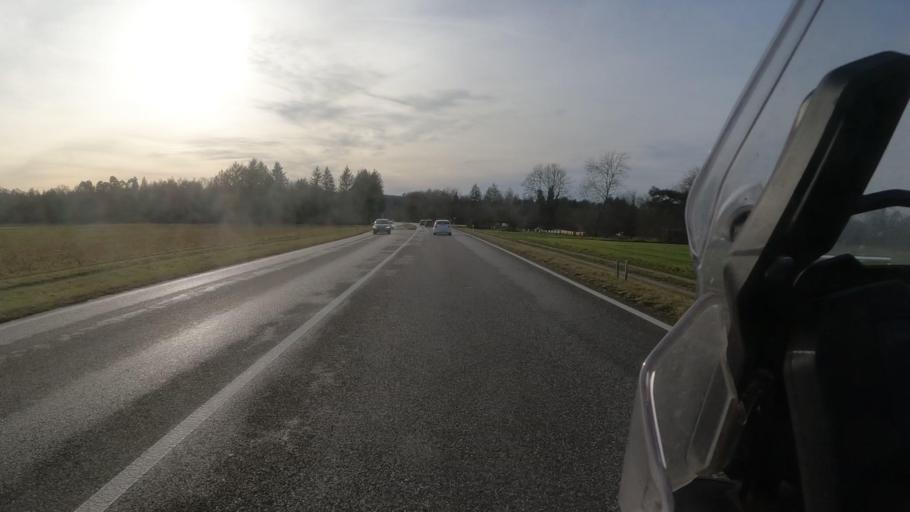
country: CH
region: Zurich
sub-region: Bezirk Buelach
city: Rafz
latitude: 47.5920
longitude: 8.5307
